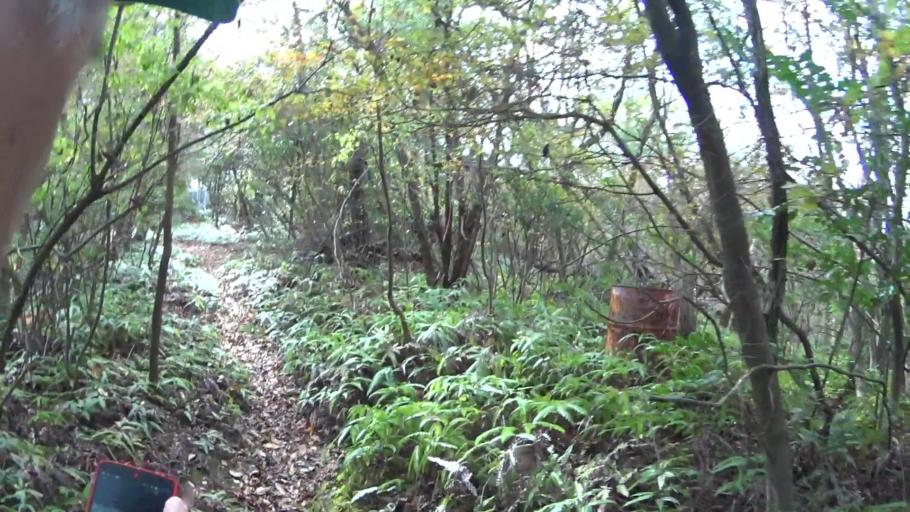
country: JP
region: Kyoto
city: Kyoto
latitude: 35.0338
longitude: 135.7157
